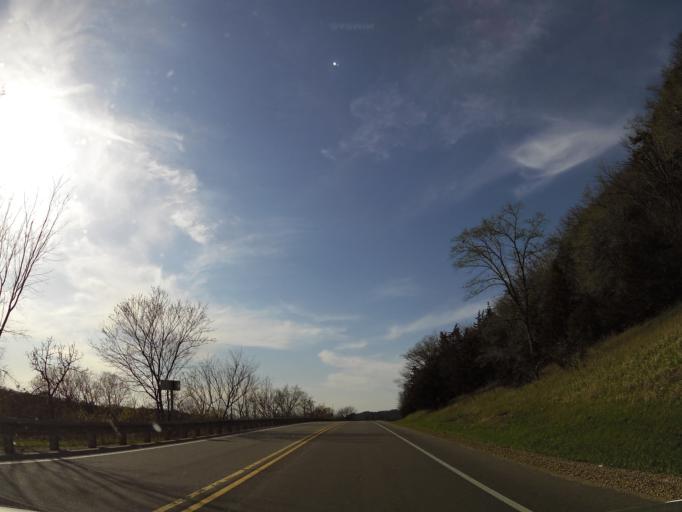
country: US
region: Minnesota
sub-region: Goodhue County
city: Red Wing
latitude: 44.6283
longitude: -92.5844
